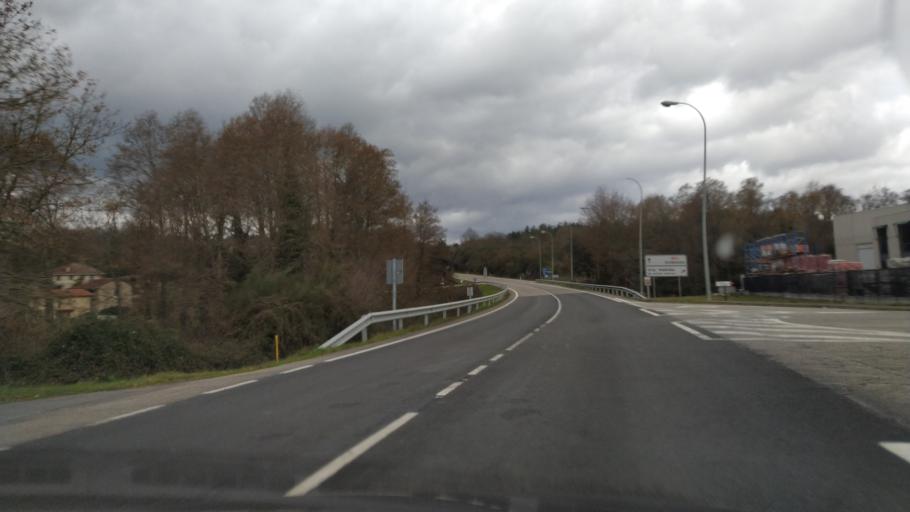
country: ES
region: Galicia
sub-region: Provincia de Ourense
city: Allariz
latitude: 42.1972
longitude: -7.8001
